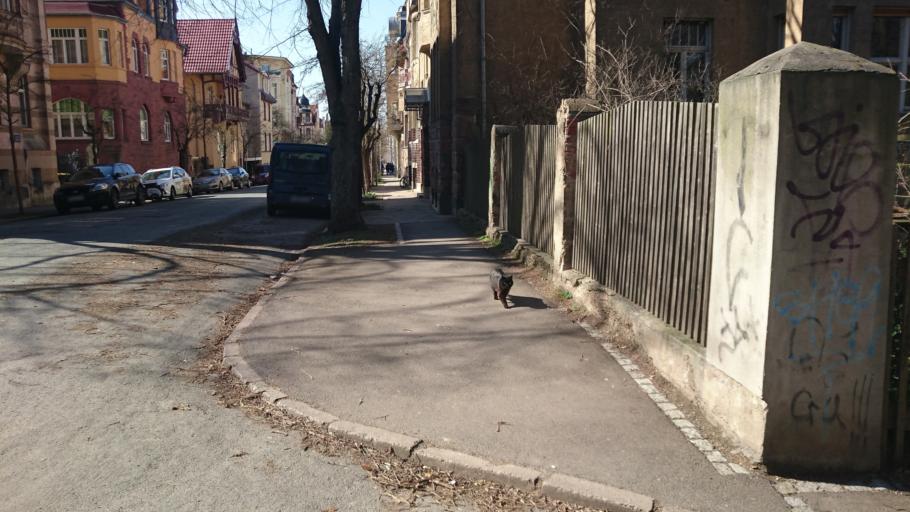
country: DE
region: Thuringia
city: Weimar
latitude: 50.9732
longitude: 11.3242
